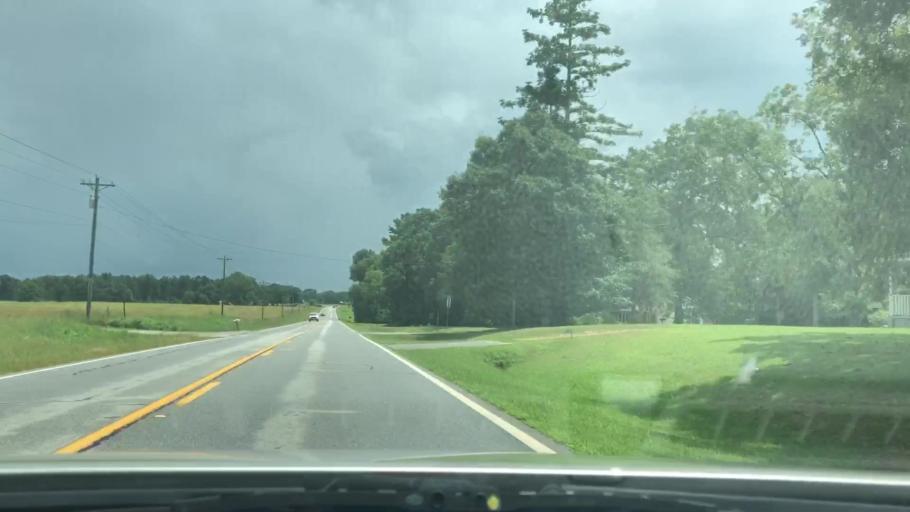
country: US
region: Georgia
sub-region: Pike County
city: Zebulon
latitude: 33.1039
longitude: -84.3033
